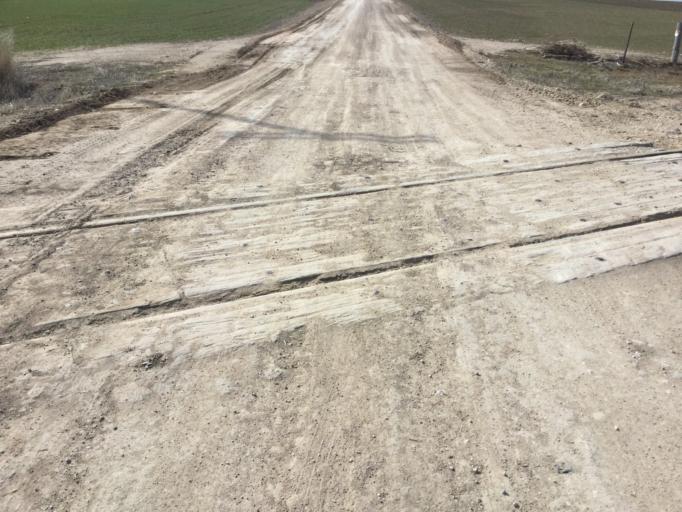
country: US
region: Kansas
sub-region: Scott County
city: Scott City
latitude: 38.5035
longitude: -100.8520
